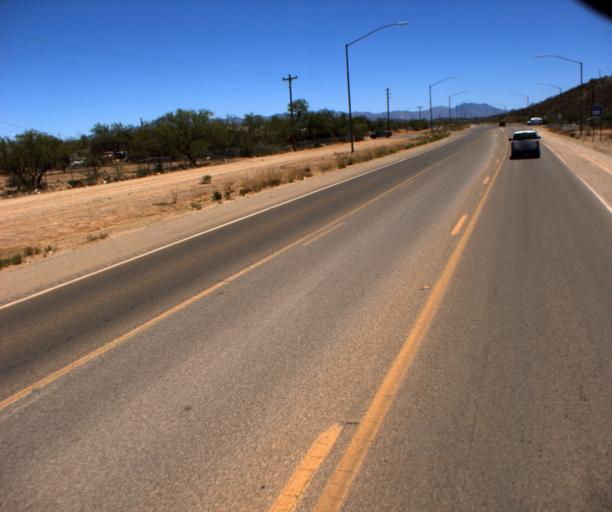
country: US
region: Arizona
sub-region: Pima County
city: Sells
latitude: 31.9220
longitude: -111.8922
